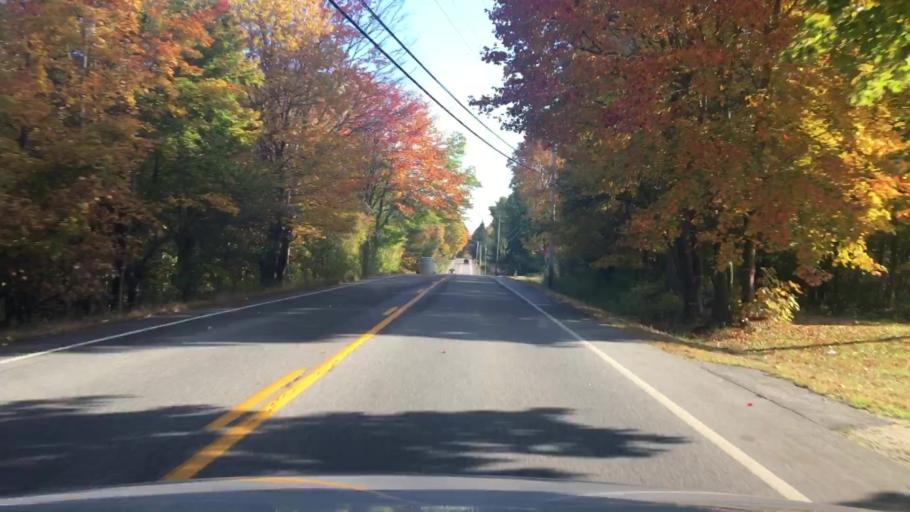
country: US
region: Maine
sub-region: Cumberland County
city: Gorham
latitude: 43.6312
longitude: -70.4479
